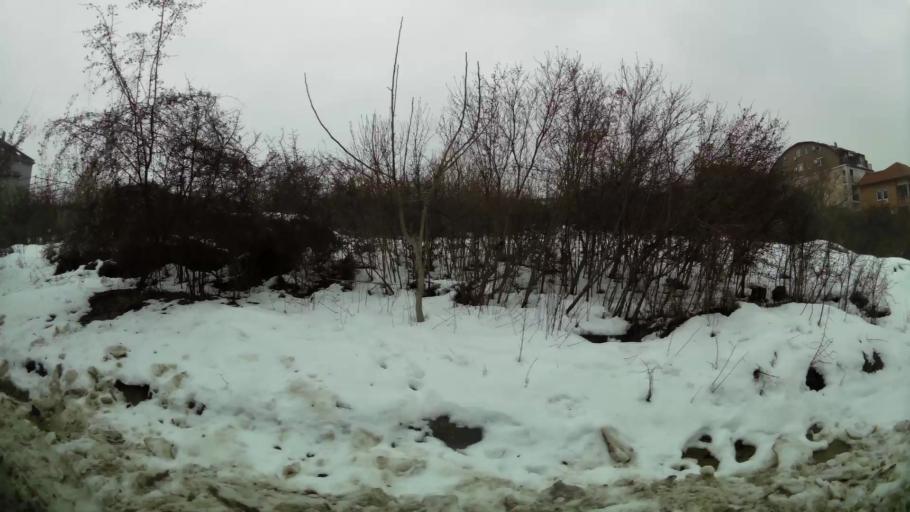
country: RS
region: Central Serbia
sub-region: Belgrade
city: Zvezdara
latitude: 44.7667
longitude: 20.5118
